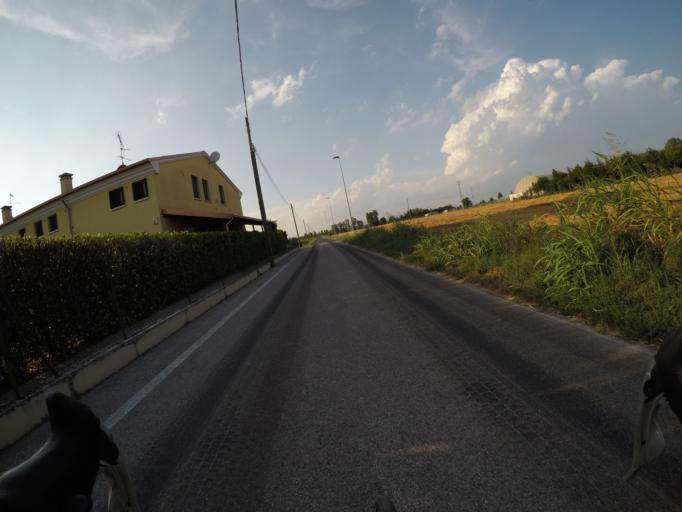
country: IT
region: Veneto
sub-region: Provincia di Rovigo
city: San Bellino
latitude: 45.0298
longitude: 11.5856
